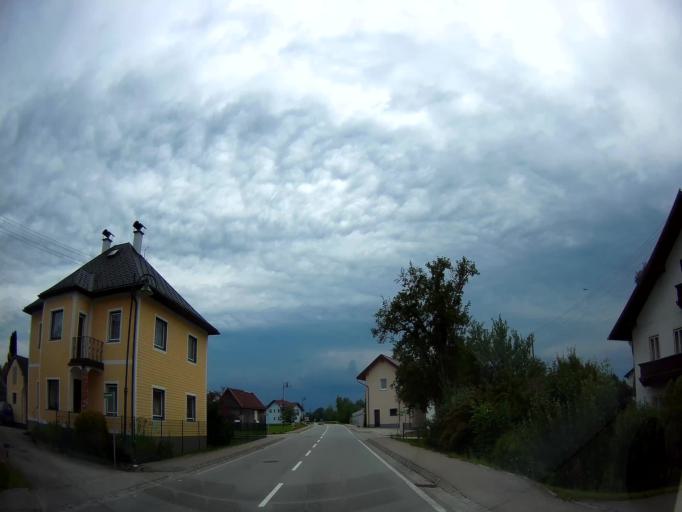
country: AT
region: Upper Austria
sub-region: Politischer Bezirk Braunau am Inn
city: Altheim
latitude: 48.2326
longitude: 13.1755
